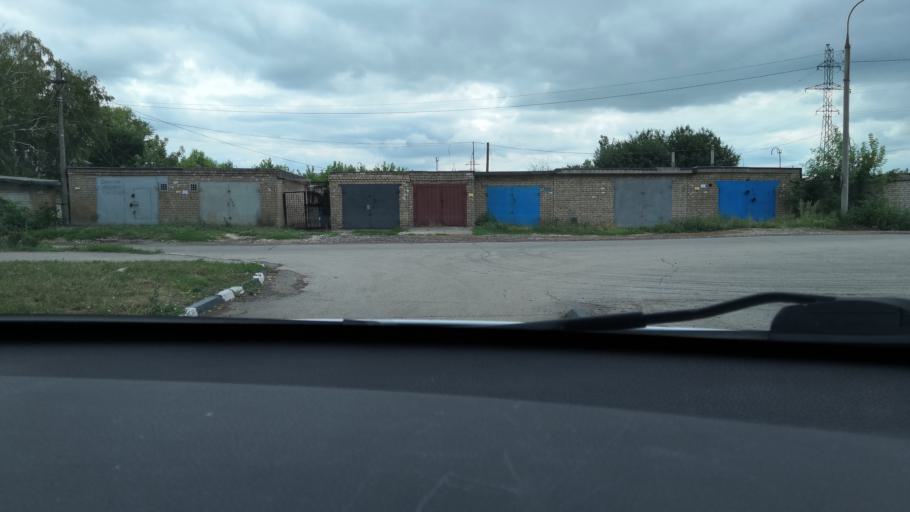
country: RU
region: Samara
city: Smyshlyayevka
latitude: 53.2691
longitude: 50.3872
